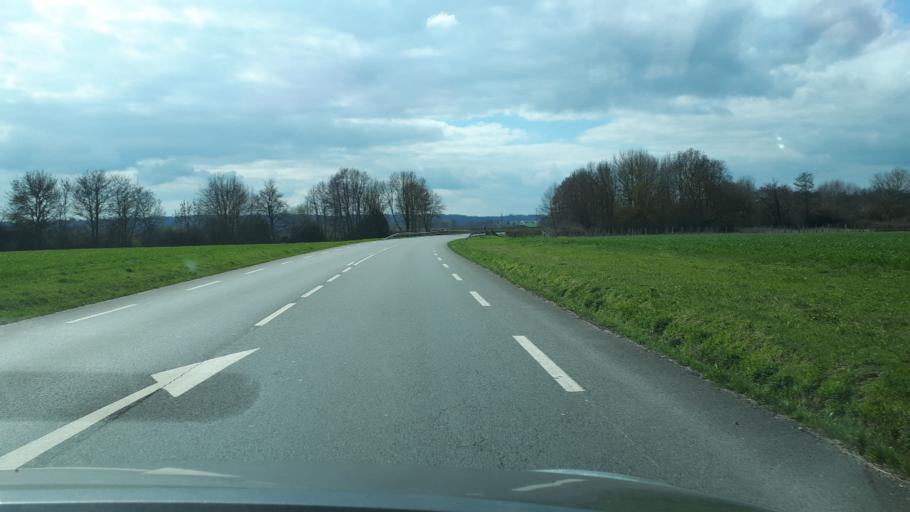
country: FR
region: Centre
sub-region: Departement du Loir-et-Cher
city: Montoire-sur-le-Loir
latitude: 47.7662
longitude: 0.9044
